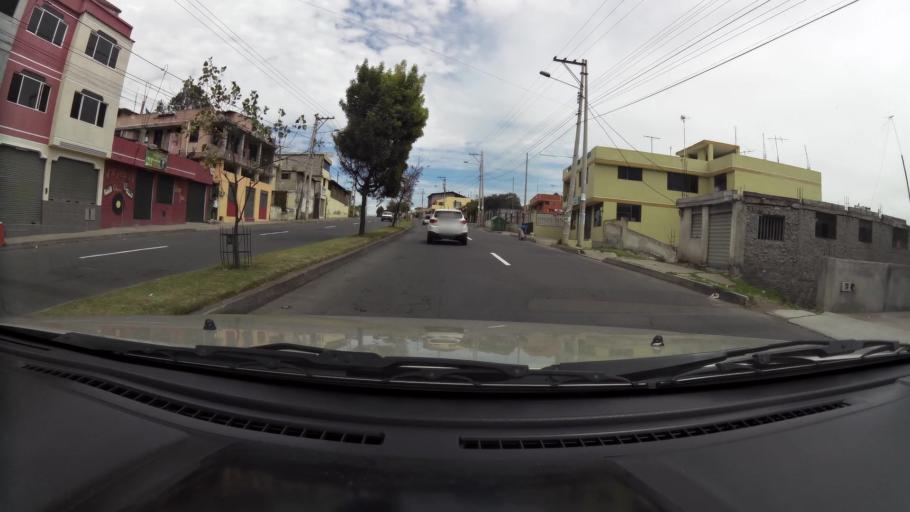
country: EC
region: Tungurahua
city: Pillaro
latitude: -1.1264
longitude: -78.5888
